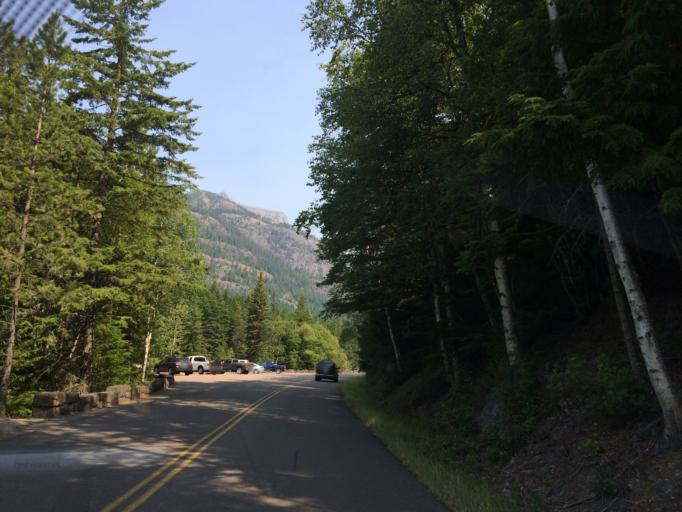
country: US
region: Montana
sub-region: Flathead County
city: Columbia Falls
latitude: 48.6552
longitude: -113.8400
